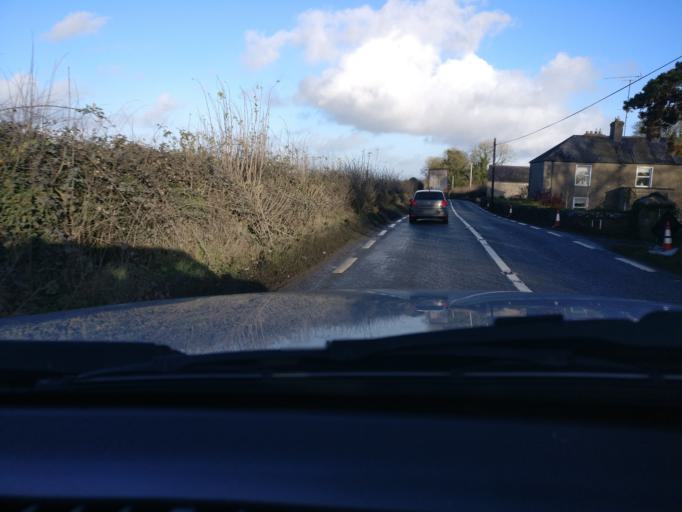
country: IE
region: Leinster
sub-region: An Iarmhi
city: Rathwire
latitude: 53.5825
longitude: -7.1408
